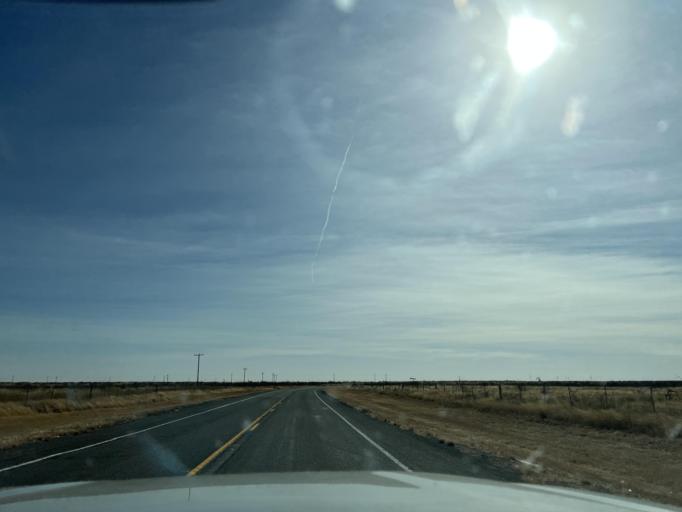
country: US
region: Texas
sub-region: Andrews County
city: Andrews
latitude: 32.4397
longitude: -102.4415
